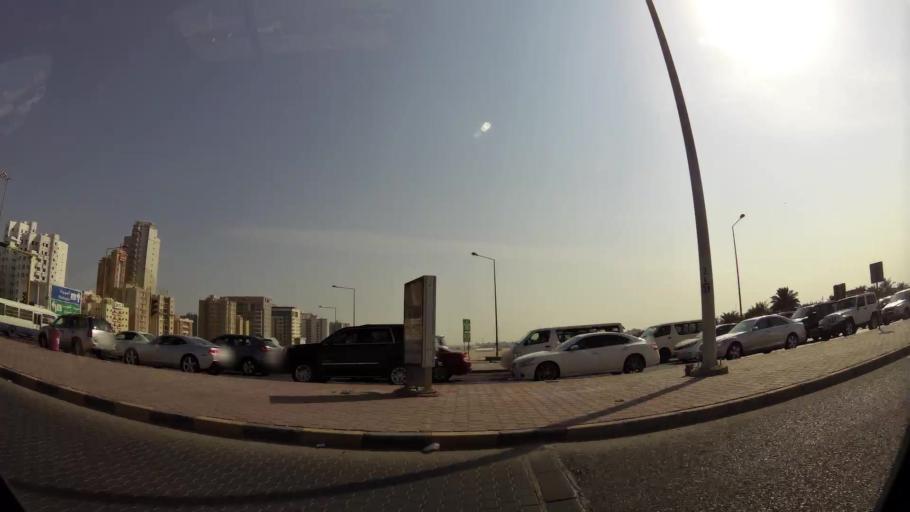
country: KW
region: Al Ahmadi
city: Al Fintas
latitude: 29.1607
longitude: 48.1096
